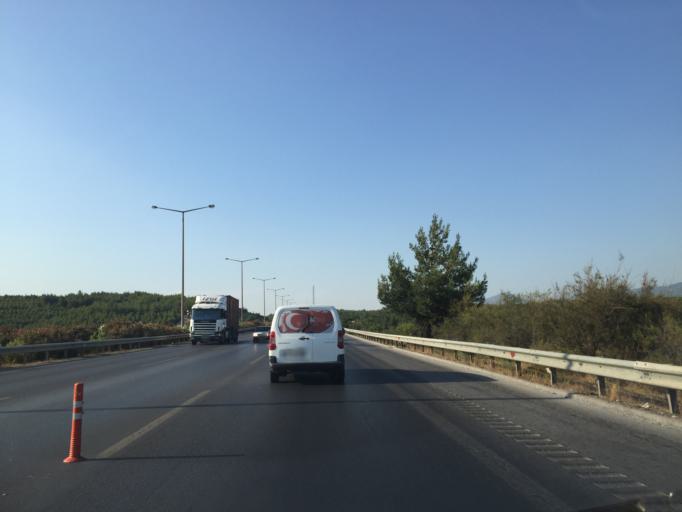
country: TR
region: Izmir
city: Menderes
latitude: 38.2812
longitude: 27.2250
